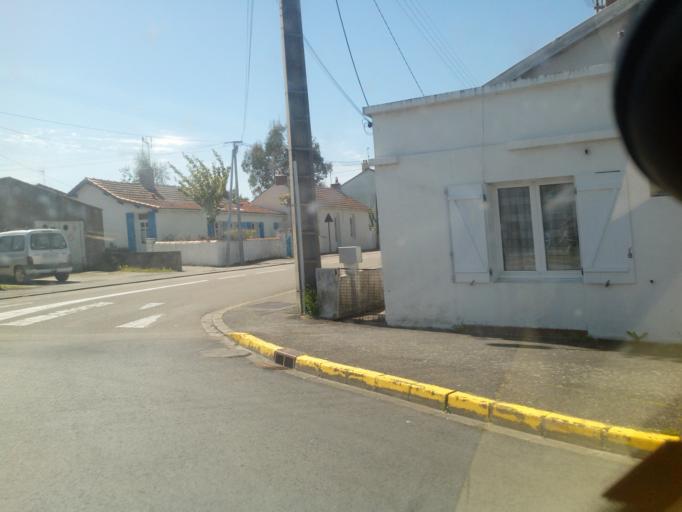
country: FR
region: Pays de la Loire
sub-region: Departement de la Loire-Atlantique
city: Pornic
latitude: 47.1097
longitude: -2.0883
